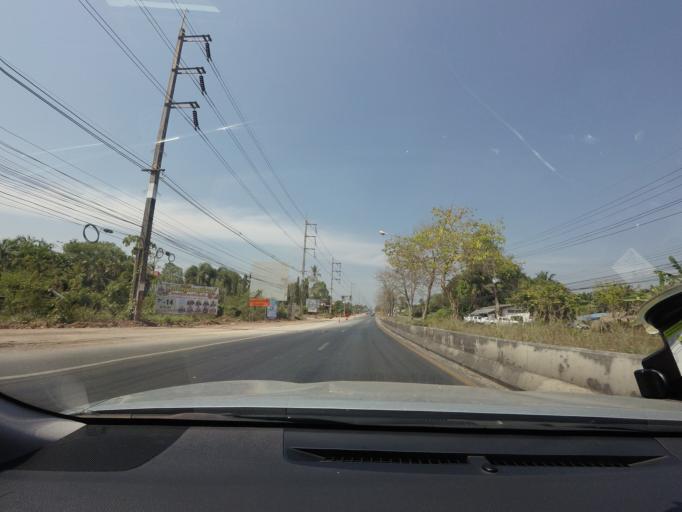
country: TH
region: Surat Thani
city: Kanchanadit
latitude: 9.1481
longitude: 99.4121
